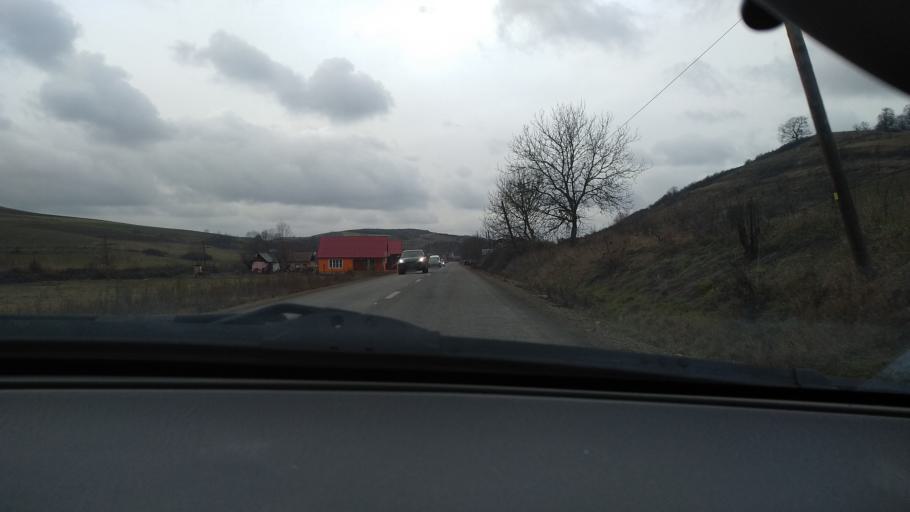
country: RO
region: Mures
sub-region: Comuna Galesti
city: Galesti
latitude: 46.5438
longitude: 24.7468
